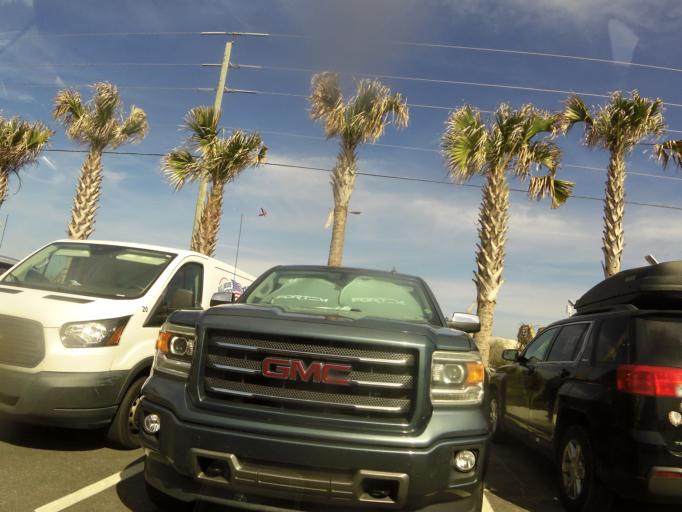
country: US
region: Florida
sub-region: Saint Johns County
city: Villano Beach
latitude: 29.9322
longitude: -81.2979
